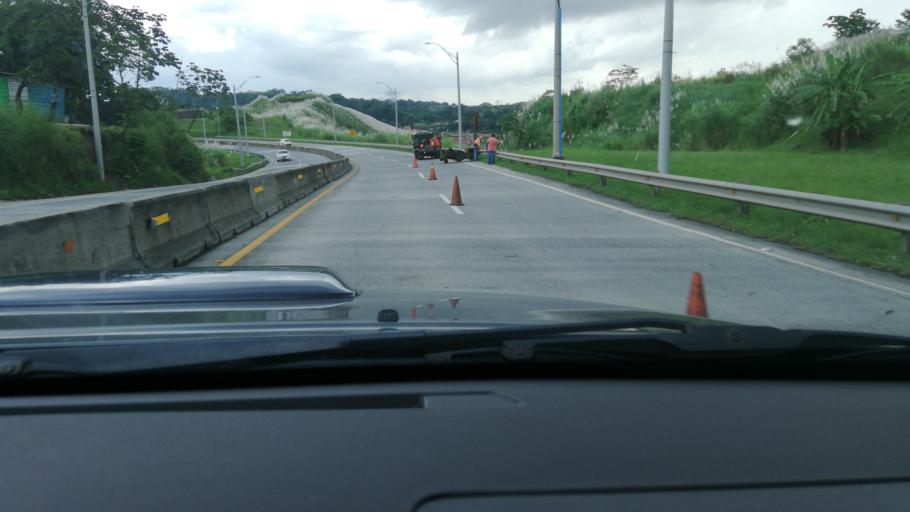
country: PA
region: Panama
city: San Miguelito
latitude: 9.0601
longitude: -79.4796
